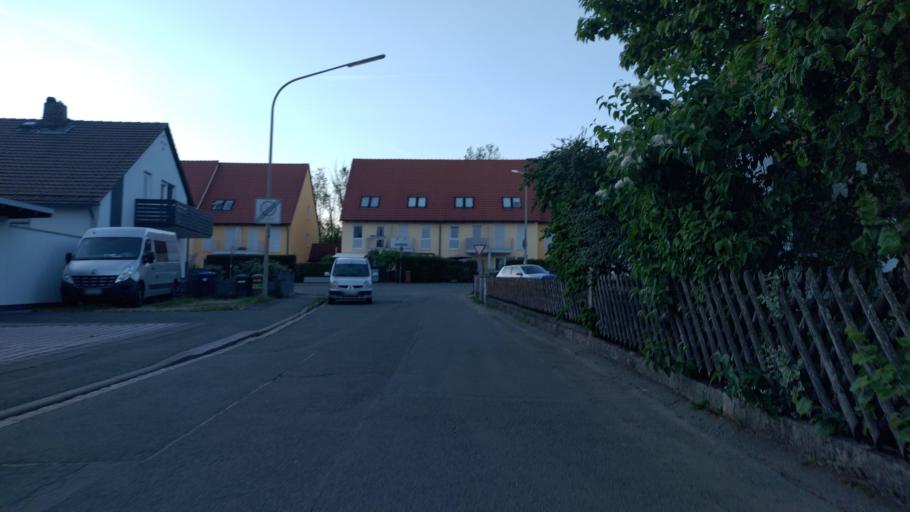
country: DE
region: Bavaria
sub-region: Upper Franconia
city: Bindlach
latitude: 49.9618
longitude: 11.6272
